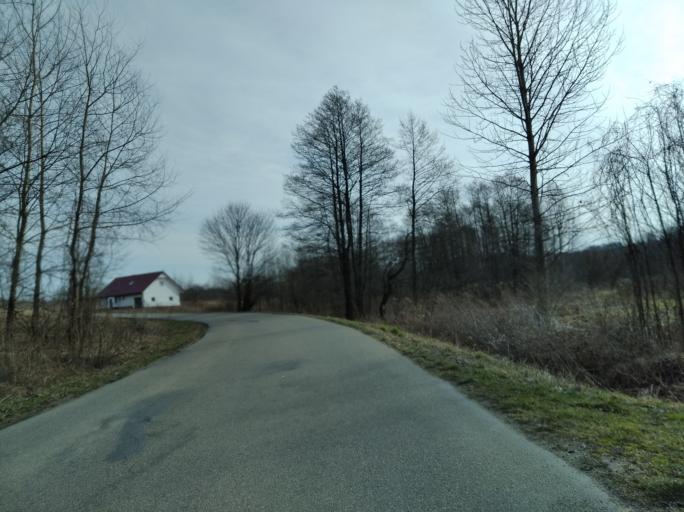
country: PL
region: Subcarpathian Voivodeship
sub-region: Powiat brzozowski
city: Stara Wies
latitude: 49.7162
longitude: 21.9760
